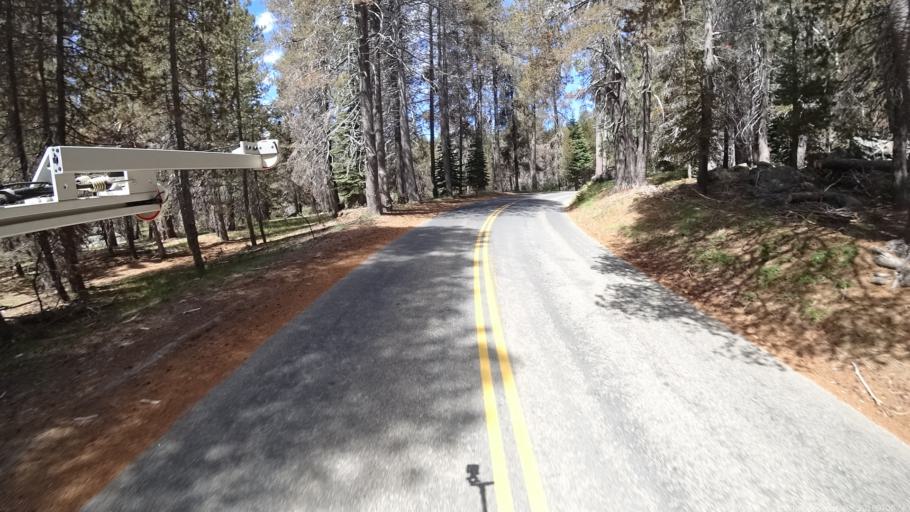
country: US
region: California
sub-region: Madera County
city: Oakhurst
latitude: 37.4463
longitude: -119.4696
